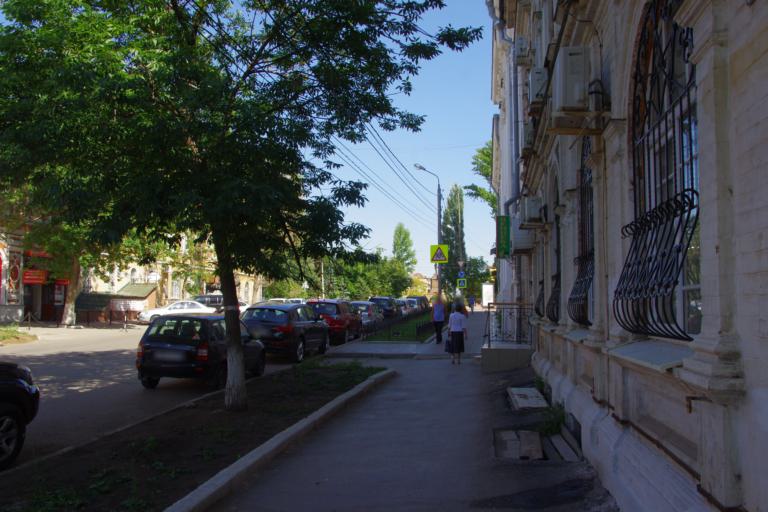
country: RU
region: Samara
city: Rozhdestveno
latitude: 53.1860
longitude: 50.0856
